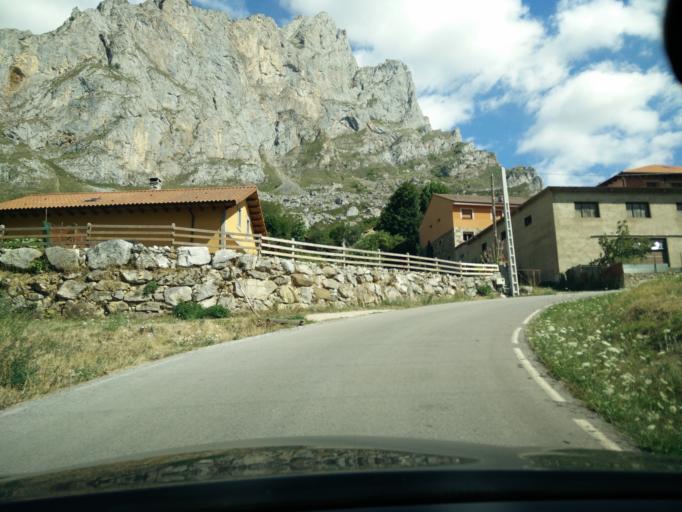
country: ES
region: Castille and Leon
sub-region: Provincia de Leon
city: Posada de Valdeon
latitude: 43.1688
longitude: -4.9041
